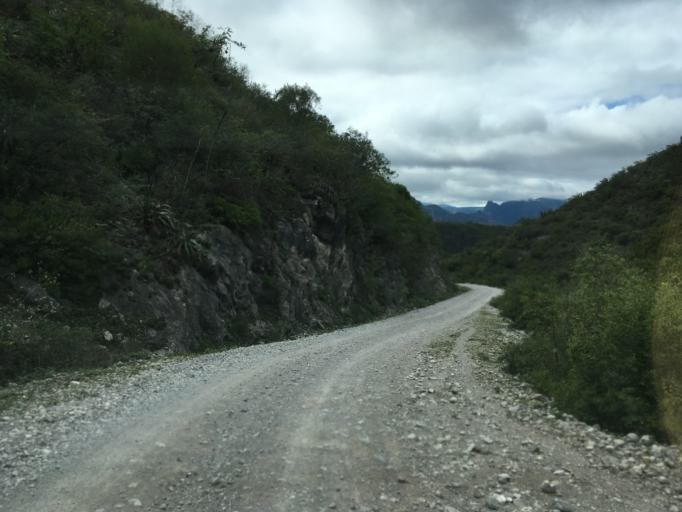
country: MX
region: Hidalgo
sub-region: Metztitlan
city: Fontezuelas
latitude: 20.6234
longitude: -98.8805
